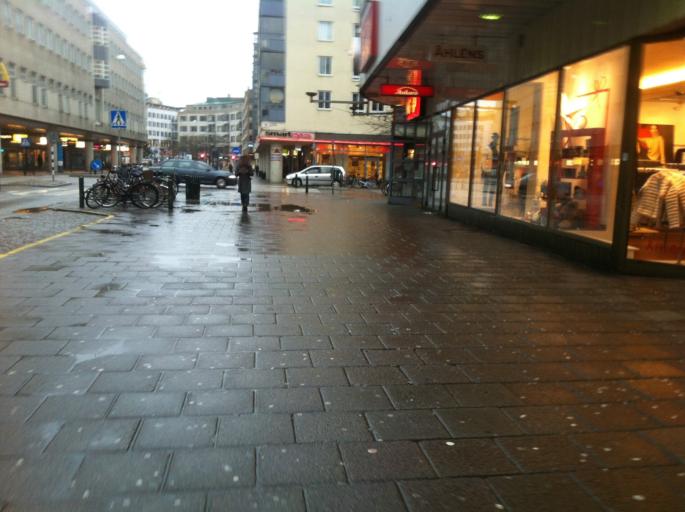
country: SE
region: Skane
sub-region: Malmo
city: Malmoe
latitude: 55.5953
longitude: 13.0032
